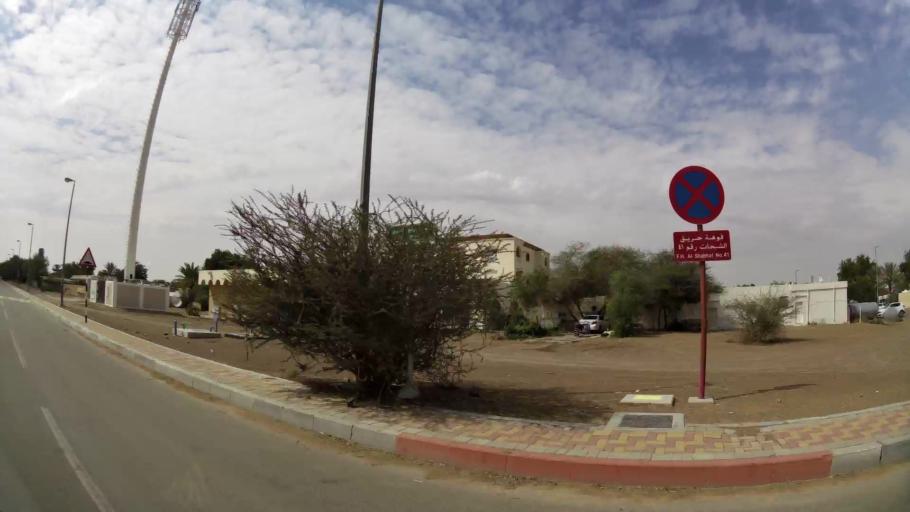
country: AE
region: Abu Dhabi
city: Al Ain
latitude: 24.1928
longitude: 55.7977
